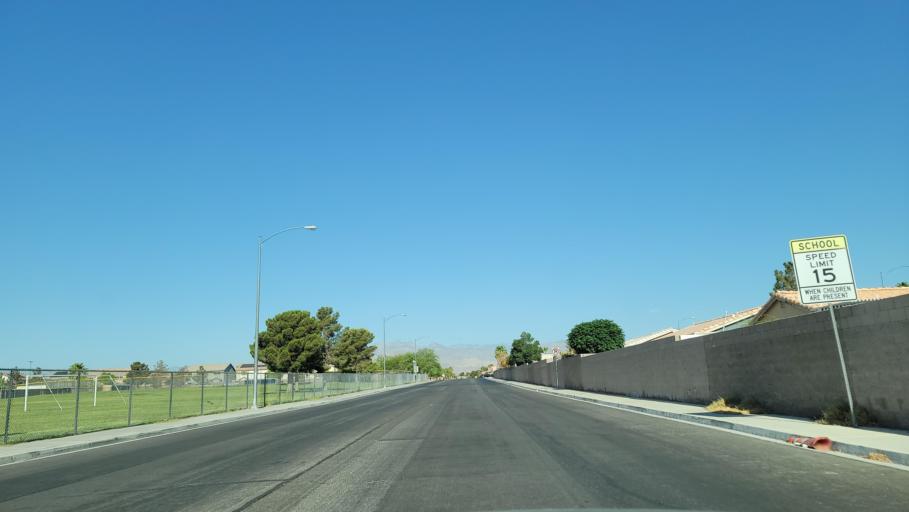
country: US
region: Nevada
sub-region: Clark County
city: North Las Vegas
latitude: 36.2358
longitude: -115.1822
